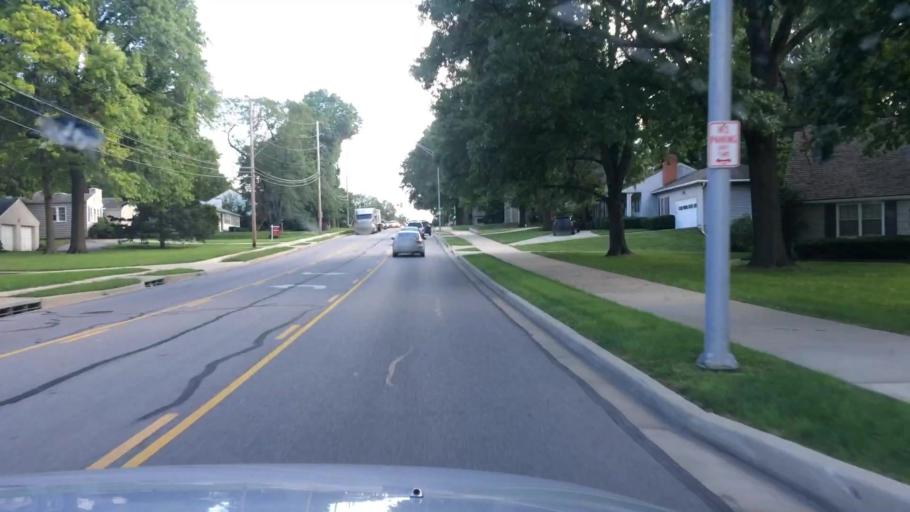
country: US
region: Kansas
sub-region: Johnson County
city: Mission
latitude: 39.0097
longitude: -94.6491
